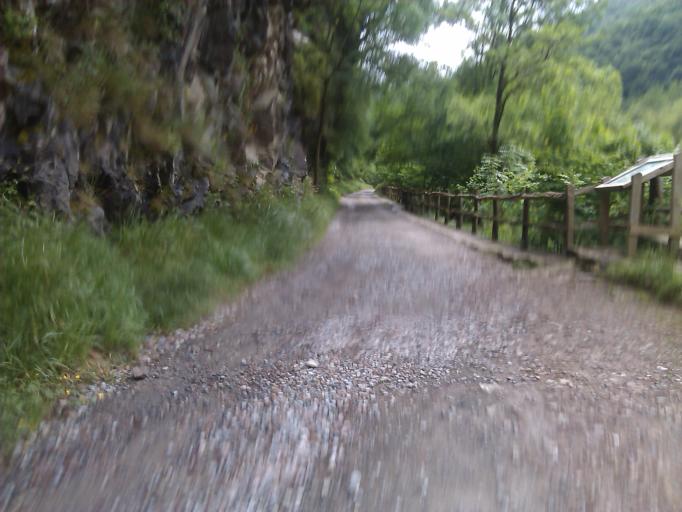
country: ES
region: Basque Country
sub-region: Provincia de Guipuzcoa
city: Elduayen
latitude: 43.1837
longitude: -1.9960
